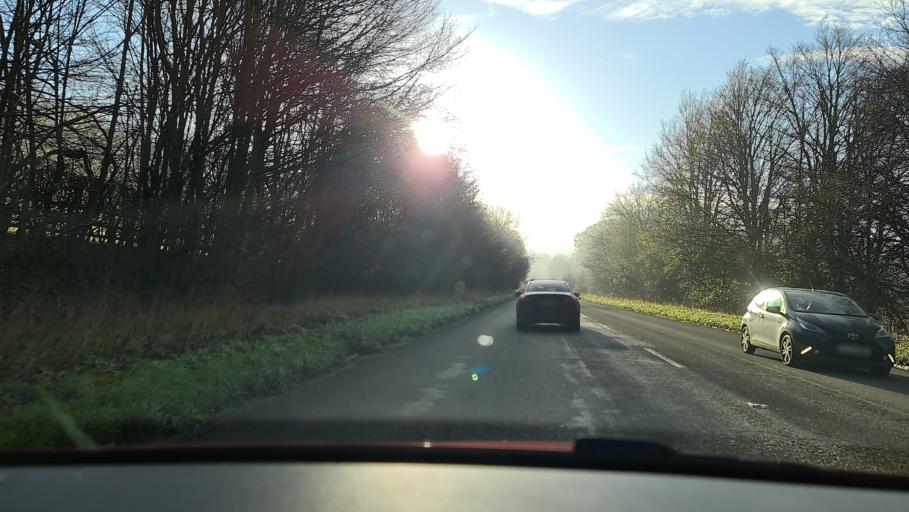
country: GB
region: England
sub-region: Buckinghamshire
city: Great Missenden
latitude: 51.6945
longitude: -0.6953
